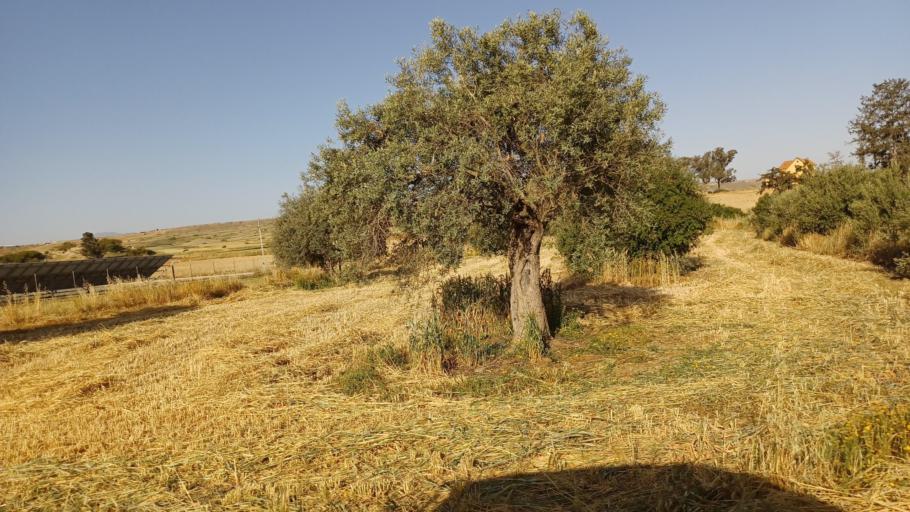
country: CY
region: Lefkosia
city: Mammari
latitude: 35.1677
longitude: 33.2489
